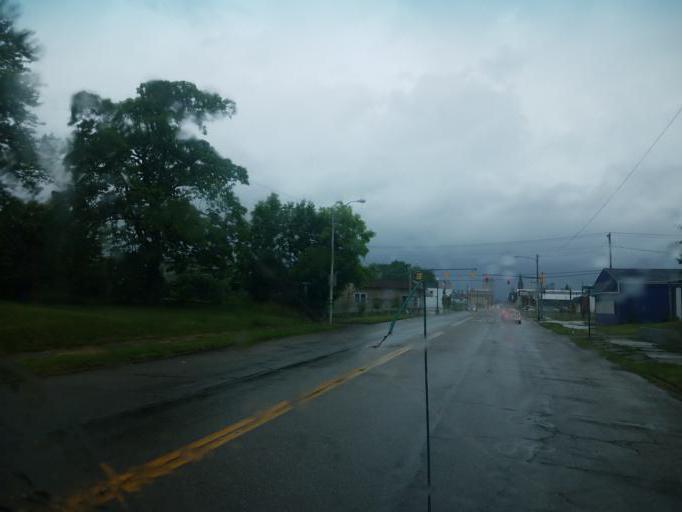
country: US
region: Ohio
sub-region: Stark County
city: Canton
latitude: 40.7957
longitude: -81.3609
